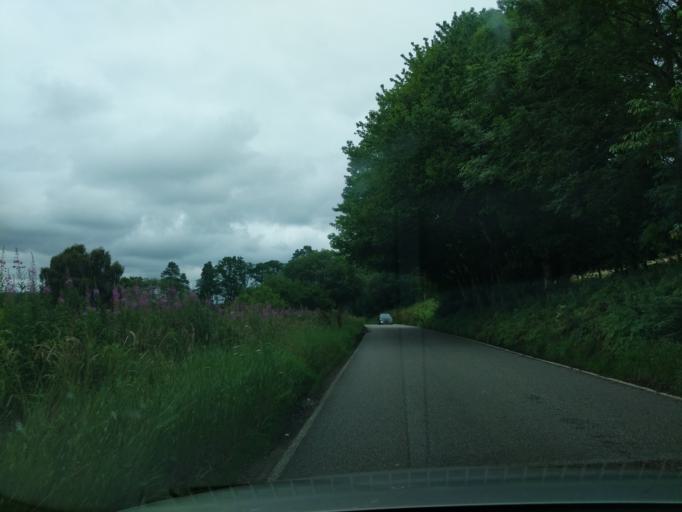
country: GB
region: Scotland
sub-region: Moray
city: Forres
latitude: 57.5165
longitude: -3.6876
